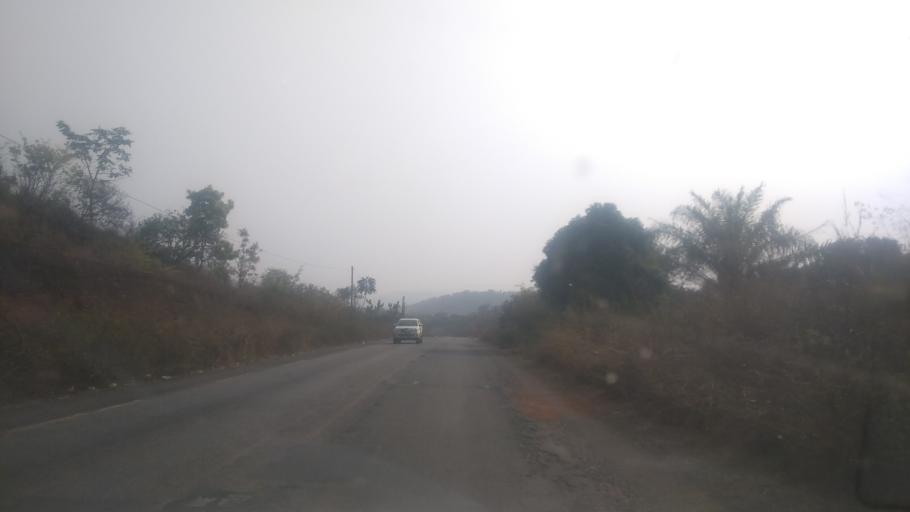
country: CM
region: West
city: Tonga
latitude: 5.0354
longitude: 10.6996
